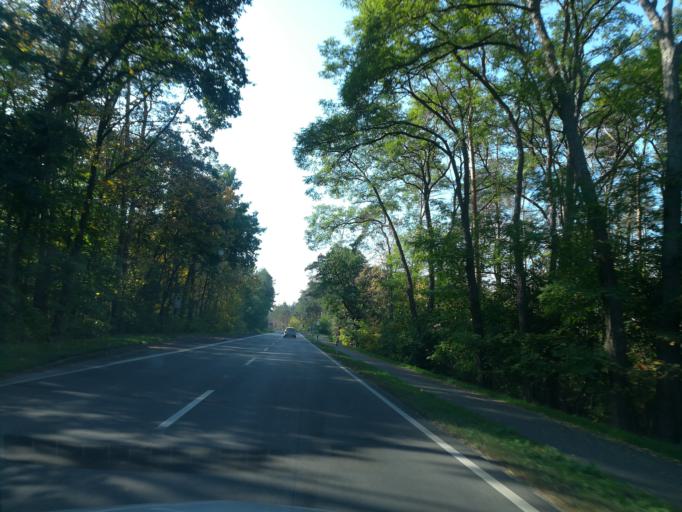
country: DE
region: Saxony-Anhalt
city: Plotzky
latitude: 52.0616
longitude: 11.8117
